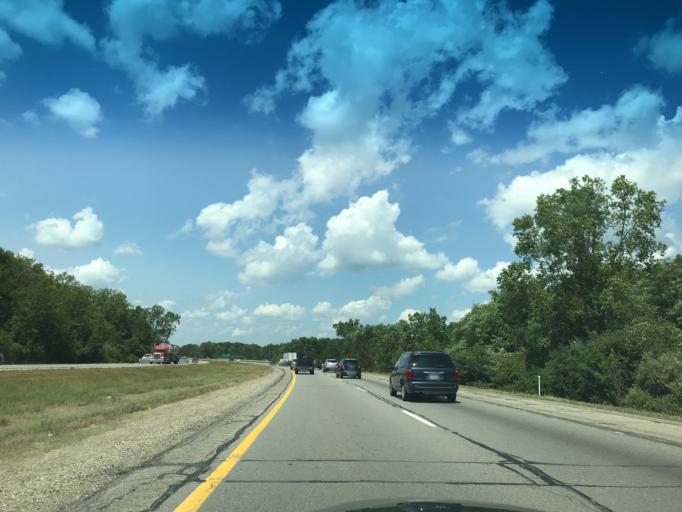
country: US
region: Michigan
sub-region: Washtenaw County
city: Ann Arbor
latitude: 42.2856
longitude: -83.6763
